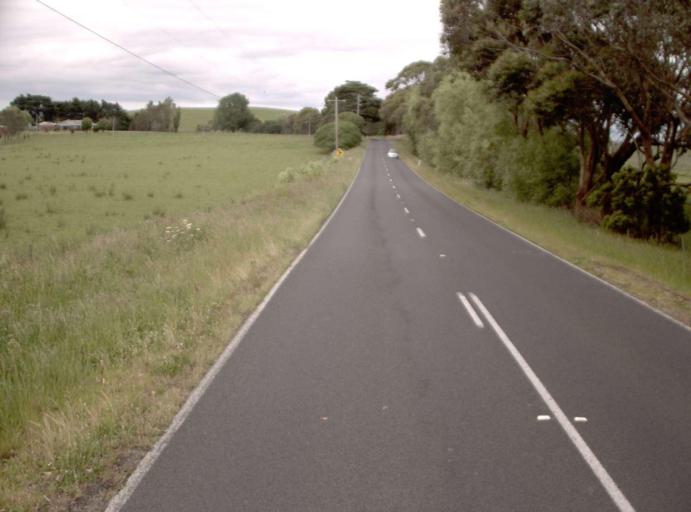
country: AU
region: Victoria
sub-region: Bass Coast
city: North Wonthaggi
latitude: -38.4914
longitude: 145.7383
